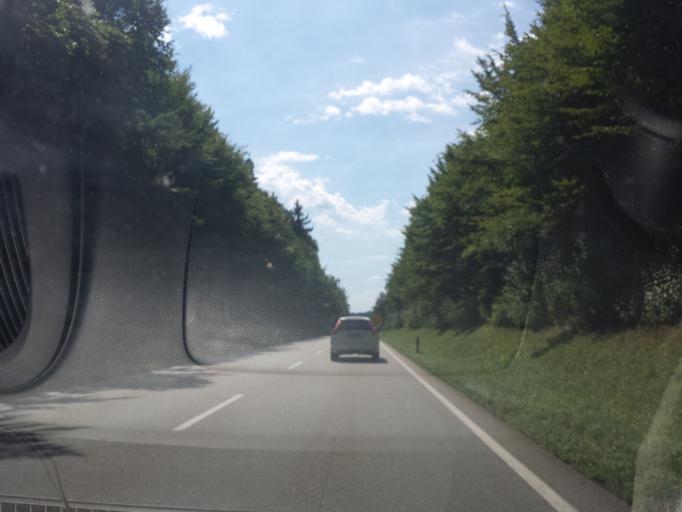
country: DE
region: Bavaria
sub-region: Lower Bavaria
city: Ascha
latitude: 49.0106
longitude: 12.6400
